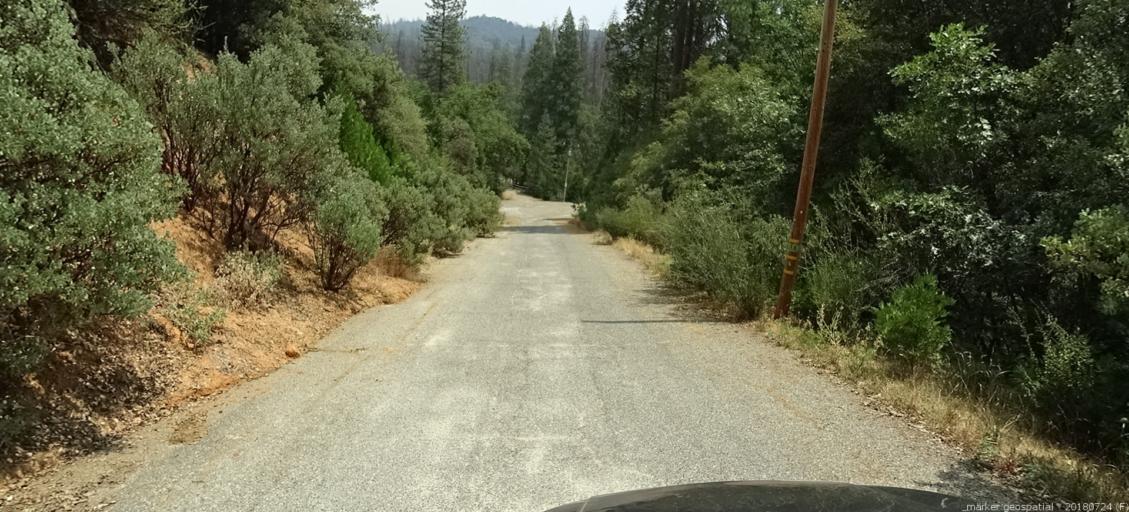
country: US
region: California
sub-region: Madera County
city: Oakhurst
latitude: 37.2677
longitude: -119.5707
